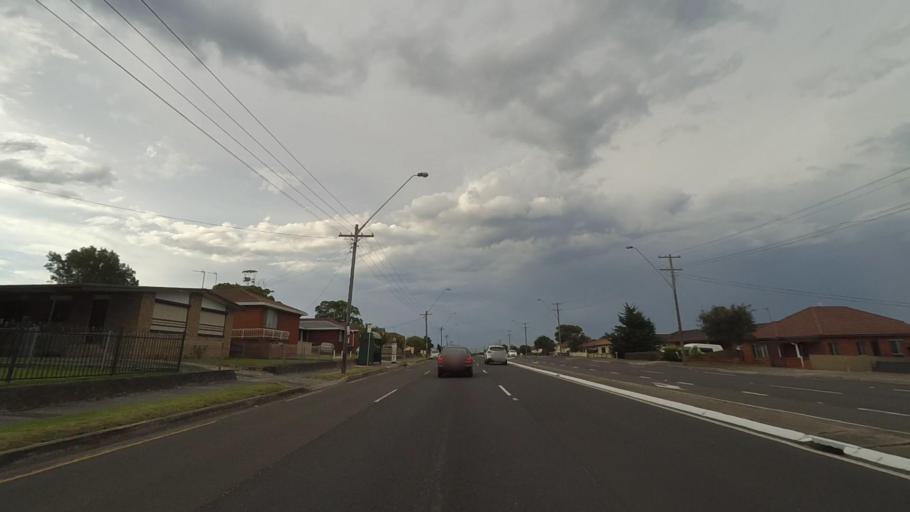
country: AU
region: New South Wales
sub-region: Shellharbour
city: Barrack Heights
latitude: -34.5645
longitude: 150.8601
